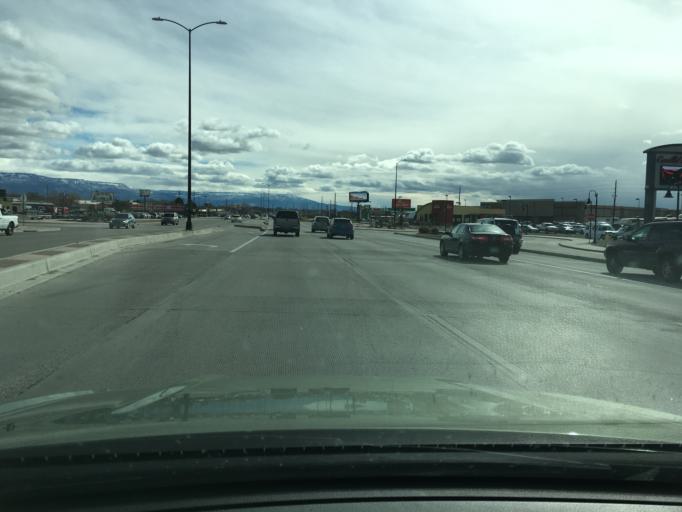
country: US
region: Colorado
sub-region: Mesa County
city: Grand Junction
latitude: 39.0826
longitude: -108.5883
